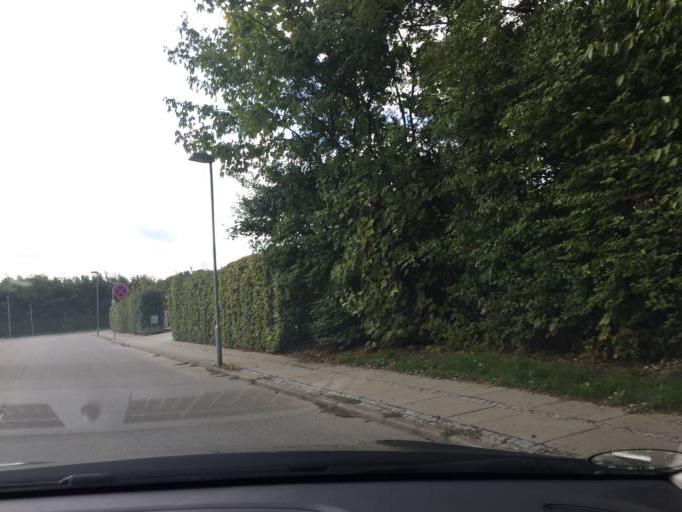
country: DK
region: Central Jutland
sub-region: Odder Kommune
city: Odder
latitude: 55.9774
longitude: 10.1630
